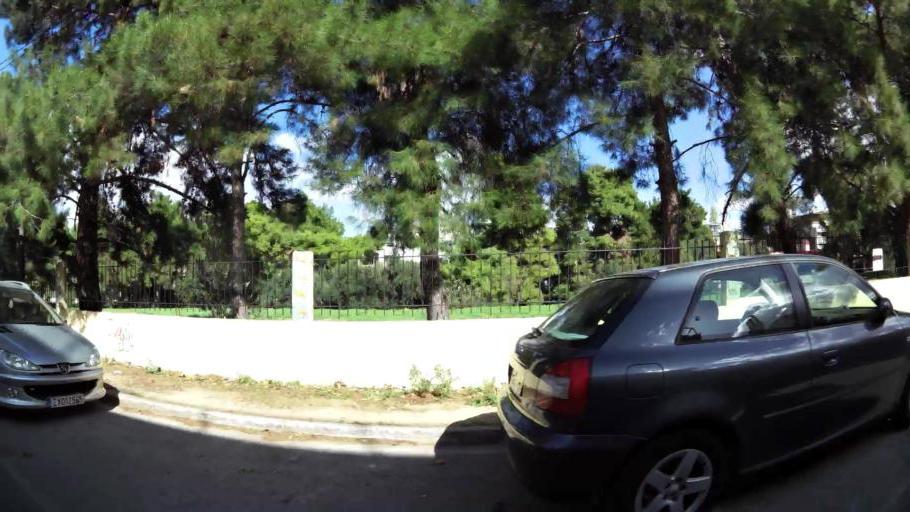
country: GR
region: Attica
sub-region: Nomarchia Athinas
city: Neo Psychiko
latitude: 38.0104
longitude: 23.7854
